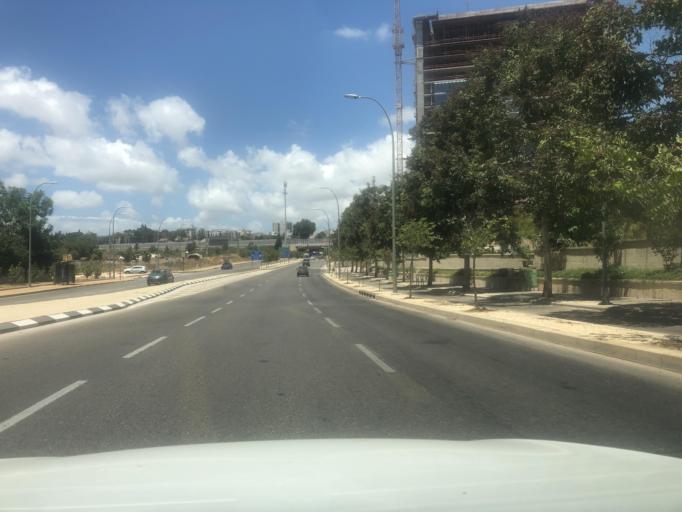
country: IL
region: Central District
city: Kfar Saba
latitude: 32.1671
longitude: 34.9014
